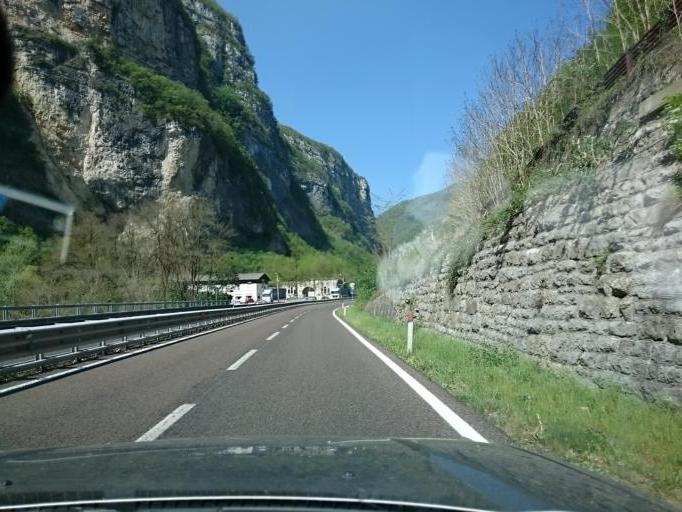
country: IT
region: Veneto
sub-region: Provincia di Vicenza
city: Cismon del Grappa
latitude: 45.9363
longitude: 11.7255
